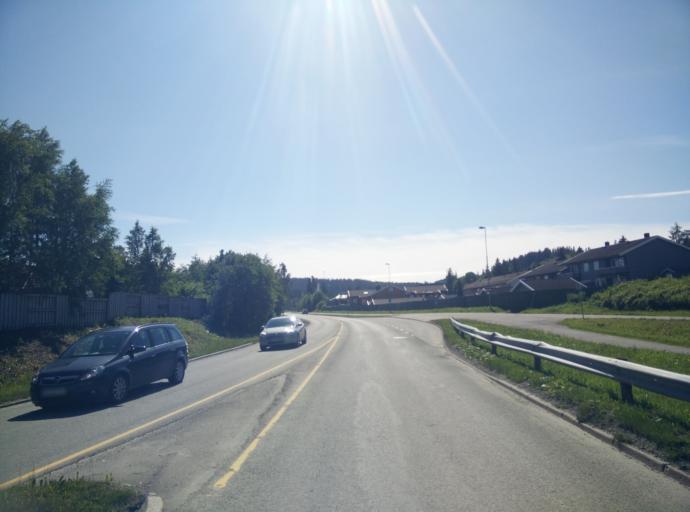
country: NO
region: Sor-Trondelag
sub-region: Trondheim
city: Trondheim
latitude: 63.3873
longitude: 10.3283
